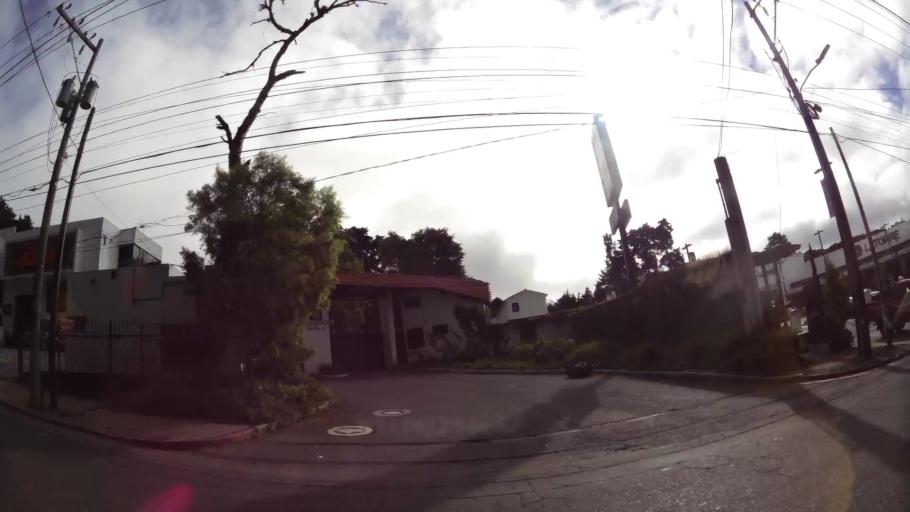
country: GT
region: Guatemala
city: Santa Catarina Pinula
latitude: 14.5603
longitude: -90.4726
